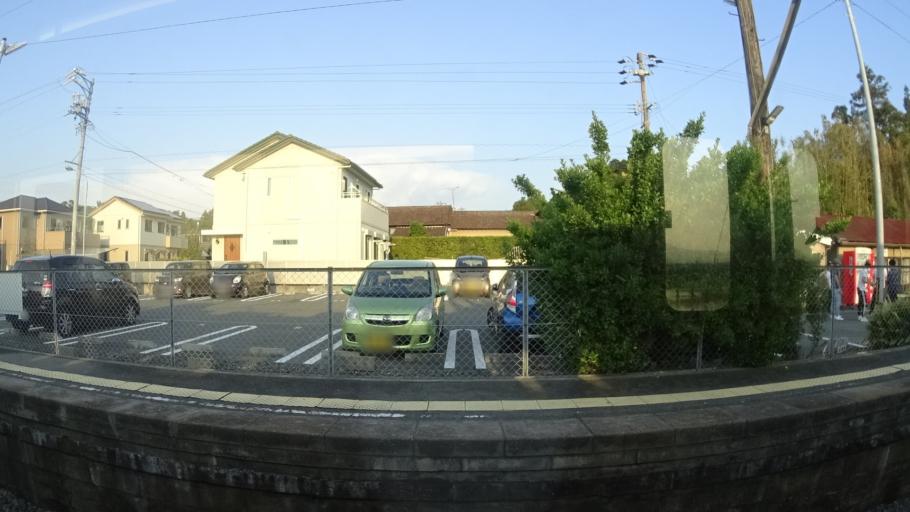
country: JP
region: Aichi
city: Tahara
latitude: 34.6804
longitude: 137.3208
